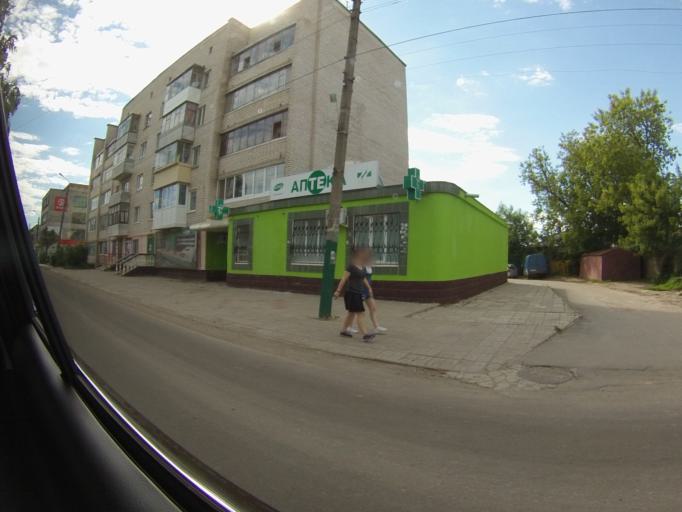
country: RU
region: Orjol
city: Mtsensk
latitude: 53.2835
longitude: 36.5806
